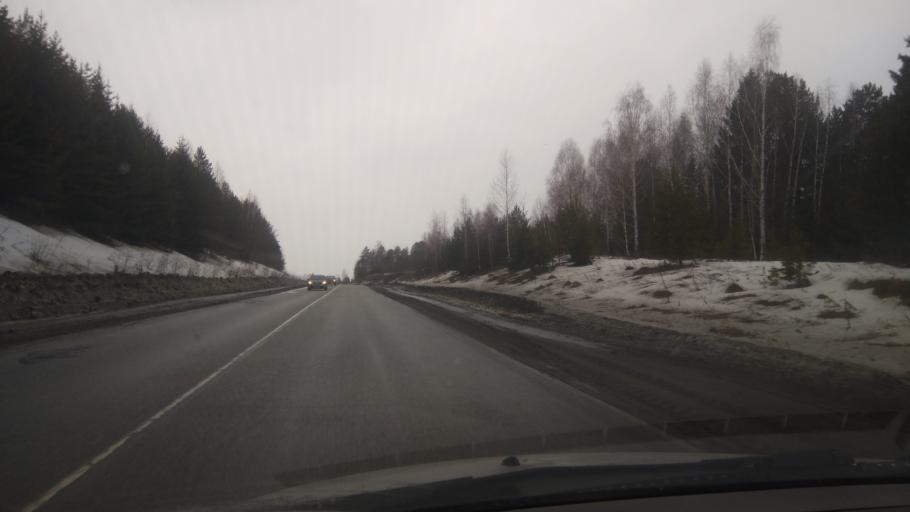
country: RU
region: Perm
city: Kungur
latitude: 57.4812
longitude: 56.7036
